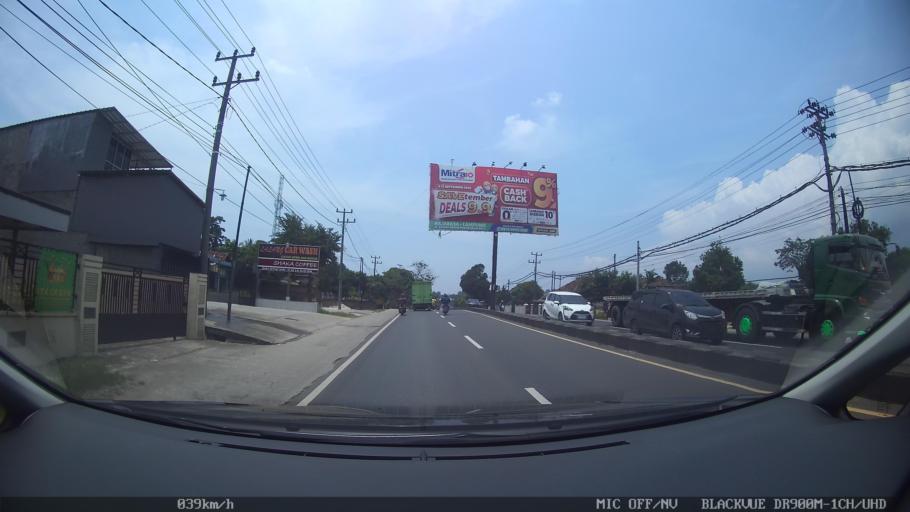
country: ID
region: Lampung
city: Natar
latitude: -5.3425
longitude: 105.2142
